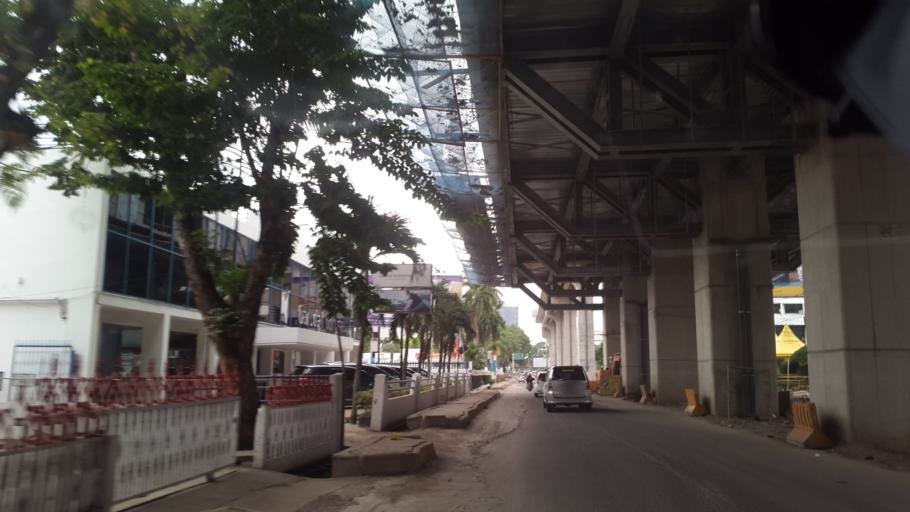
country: ID
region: South Sumatra
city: Plaju
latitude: -2.9785
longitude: 104.7492
